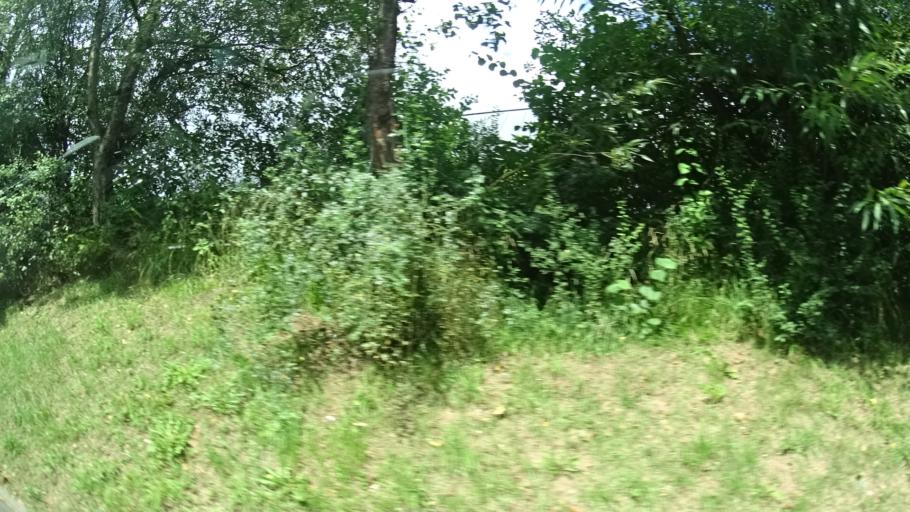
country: DE
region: Bavaria
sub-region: Upper Franconia
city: Untersiemau
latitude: 50.1816
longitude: 10.9917
